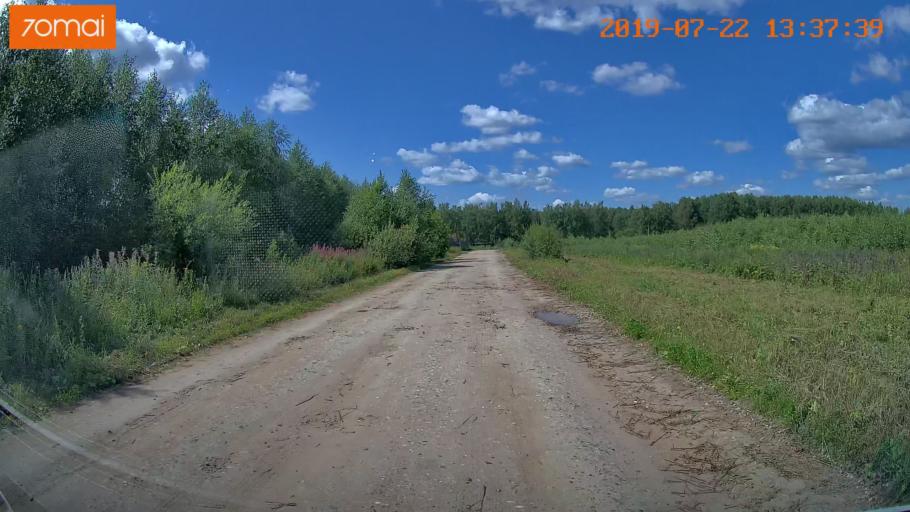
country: RU
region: Ivanovo
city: Novo-Talitsy
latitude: 57.0681
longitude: 40.8851
